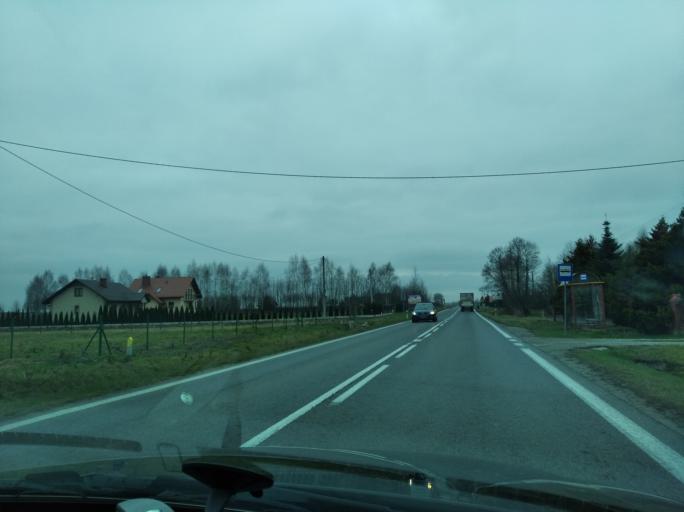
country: PL
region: Subcarpathian Voivodeship
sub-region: Powiat lancucki
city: Zolynia
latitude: 50.1784
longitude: 22.3126
